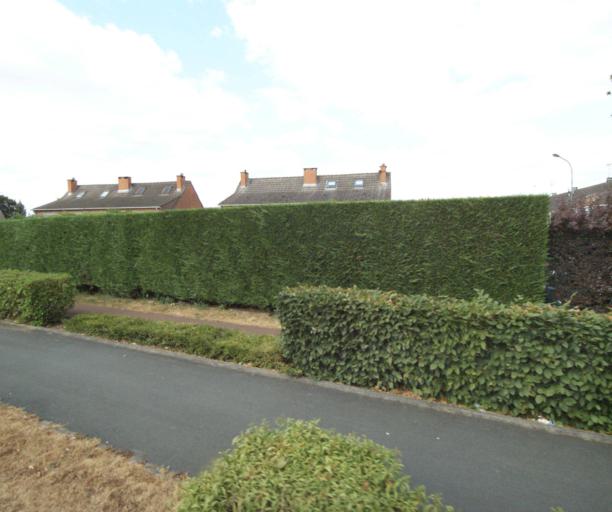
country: FR
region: Nord-Pas-de-Calais
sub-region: Departement du Nord
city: Mouvaux
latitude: 50.7077
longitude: 3.1284
